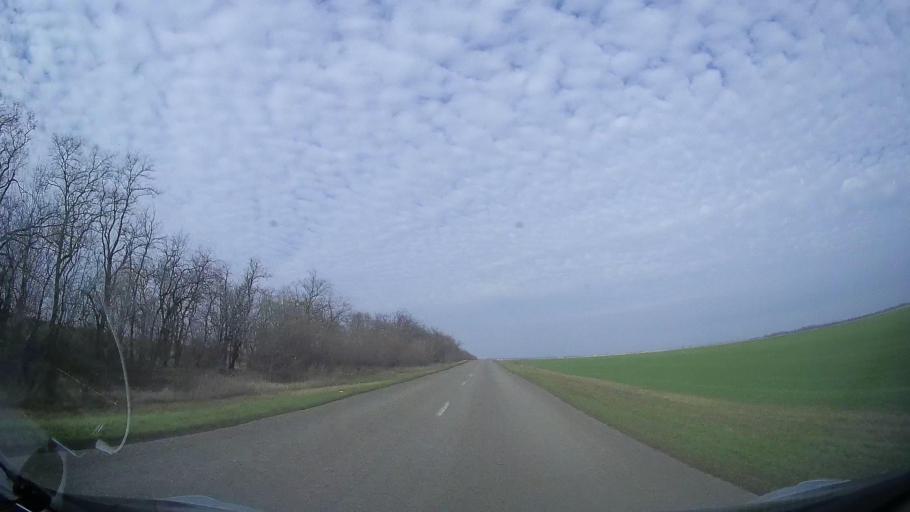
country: RU
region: Rostov
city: Gigant
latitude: 46.9329
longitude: 41.2436
